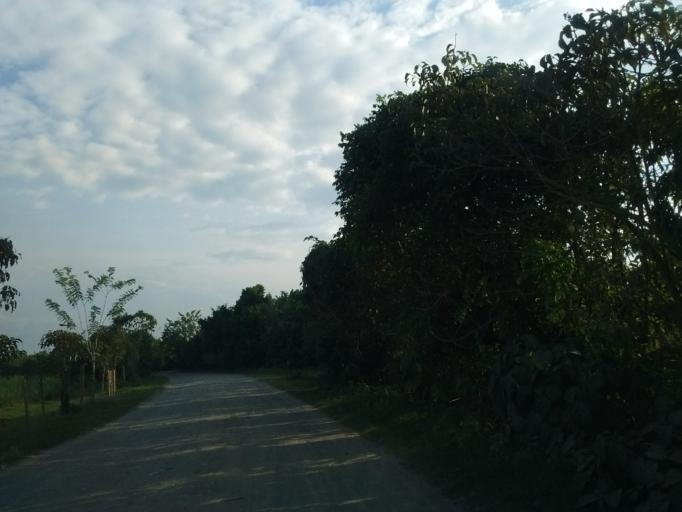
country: CO
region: Cauca
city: Puerto Tejada
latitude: 3.2215
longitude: -76.4463
